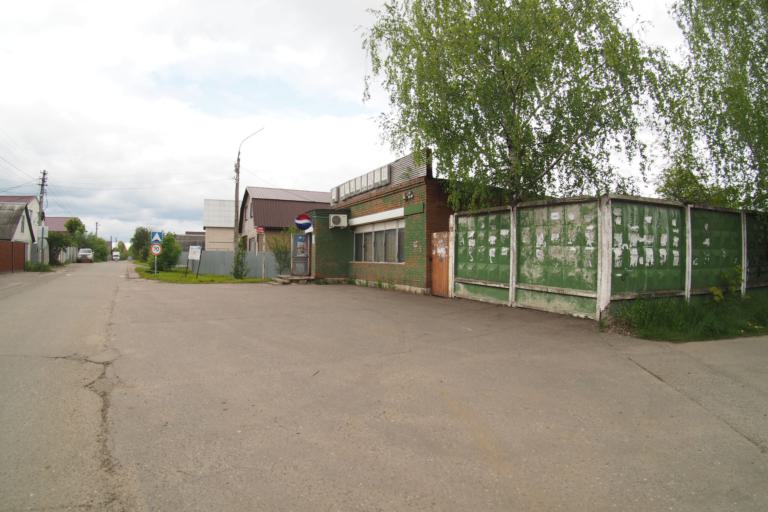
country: RU
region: Moskovskaya
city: Rechitsy
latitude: 55.5785
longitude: 38.5022
